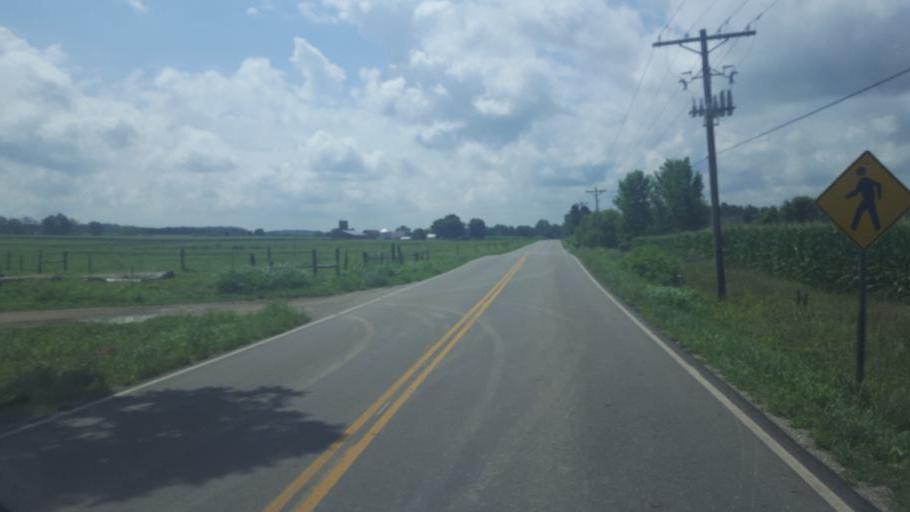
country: US
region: Ohio
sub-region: Ross County
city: Kingston
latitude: 39.5391
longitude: -82.7702
